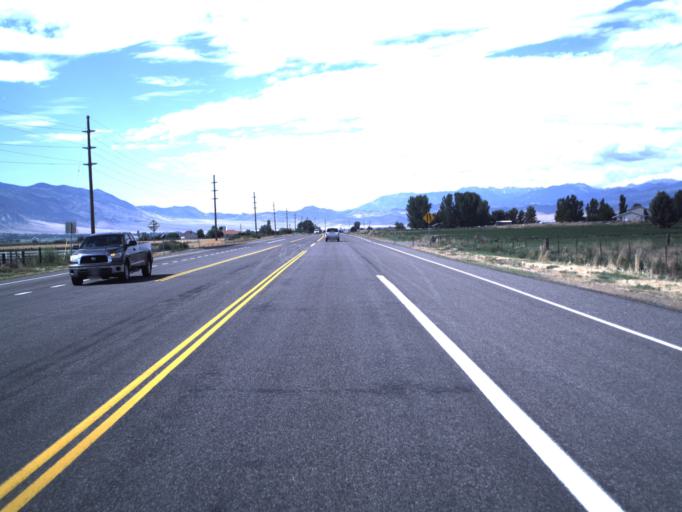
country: US
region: Utah
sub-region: Sevier County
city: Monroe
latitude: 38.7027
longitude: -112.1105
